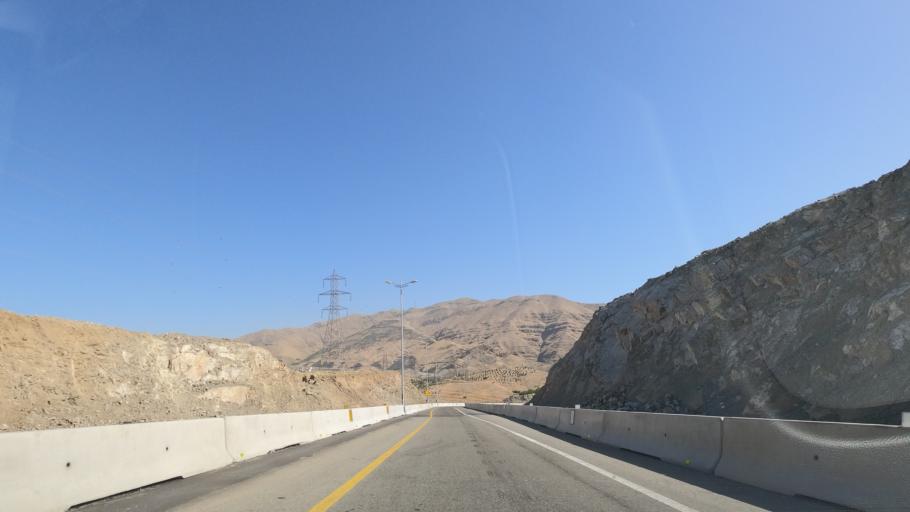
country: IR
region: Alborz
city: Karaj
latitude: 35.8204
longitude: 51.0377
